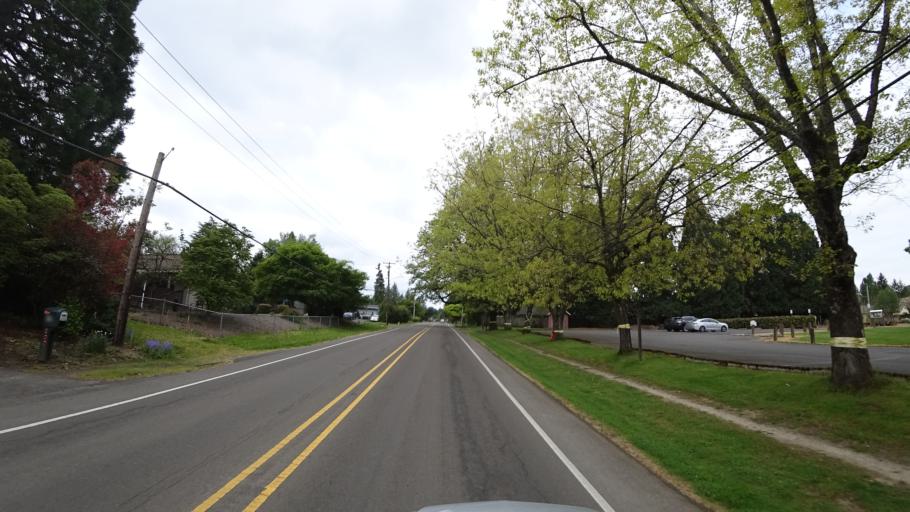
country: US
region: Oregon
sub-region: Washington County
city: Hillsboro
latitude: 45.5314
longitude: -122.9802
